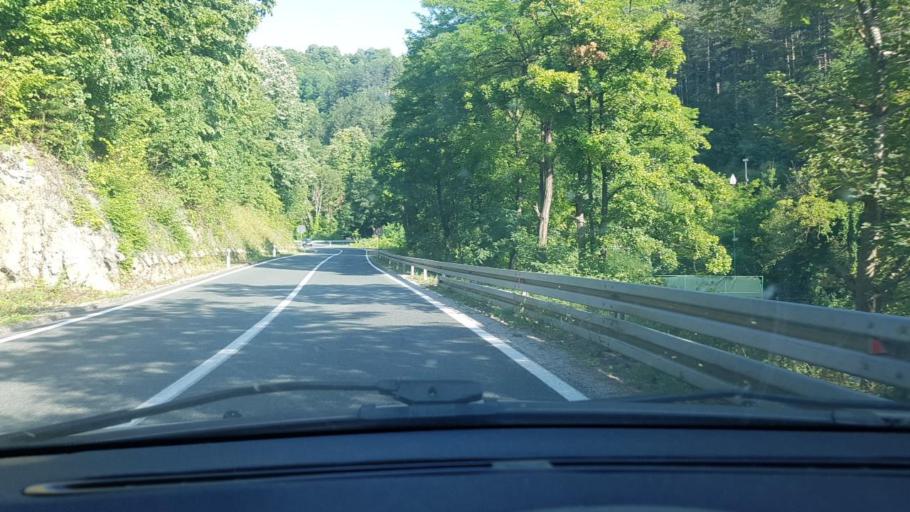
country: BA
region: Federation of Bosnia and Herzegovina
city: Ostrozac
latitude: 44.9000
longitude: 15.9359
